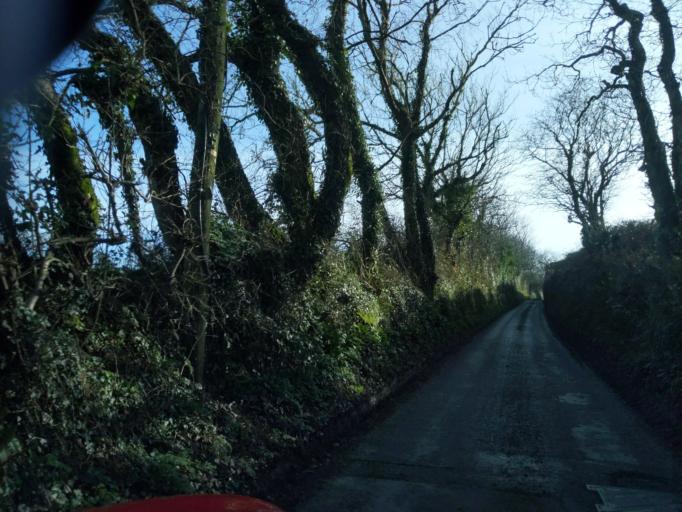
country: GB
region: England
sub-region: Devon
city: Kingsbridge
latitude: 50.3312
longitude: -3.7192
